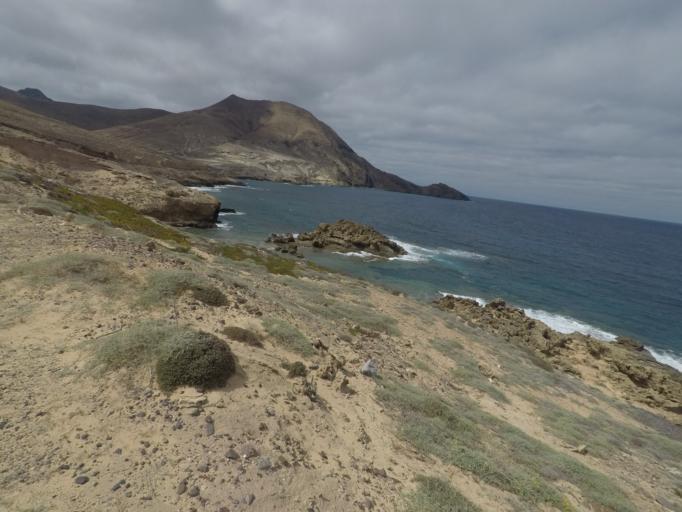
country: PT
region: Madeira
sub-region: Porto Santo
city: Vila de Porto Santo
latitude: 33.0638
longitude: -16.2955
